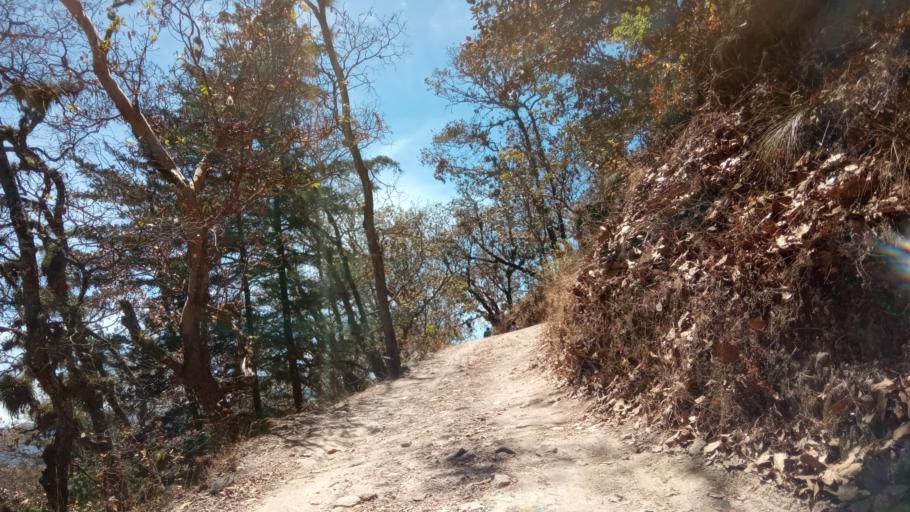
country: GT
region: San Marcos
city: Tejutla
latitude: 15.1364
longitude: -91.7919
